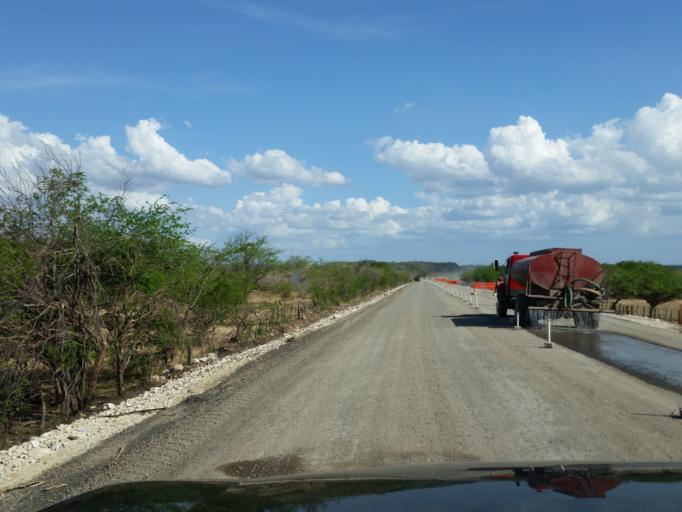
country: NI
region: Leon
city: Nagarote
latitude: 12.1952
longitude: -86.6780
